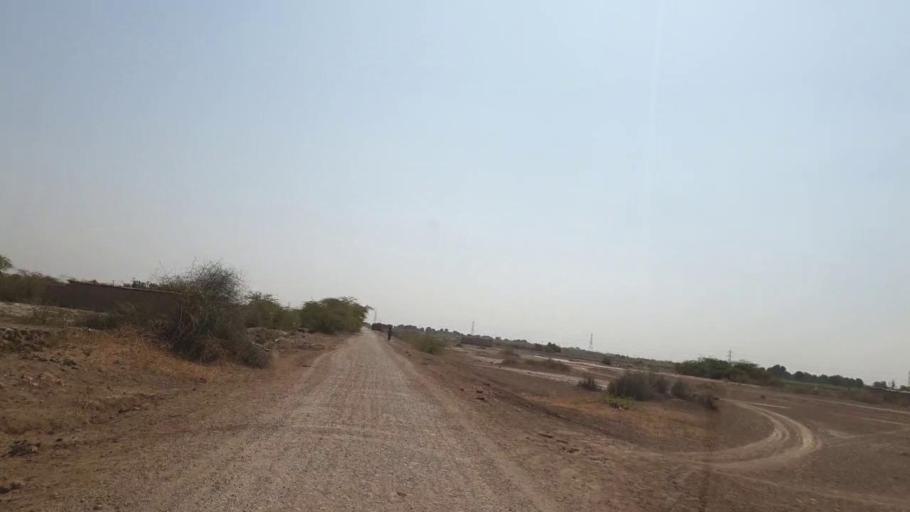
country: PK
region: Sindh
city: Nabisar
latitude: 25.0743
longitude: 69.5488
